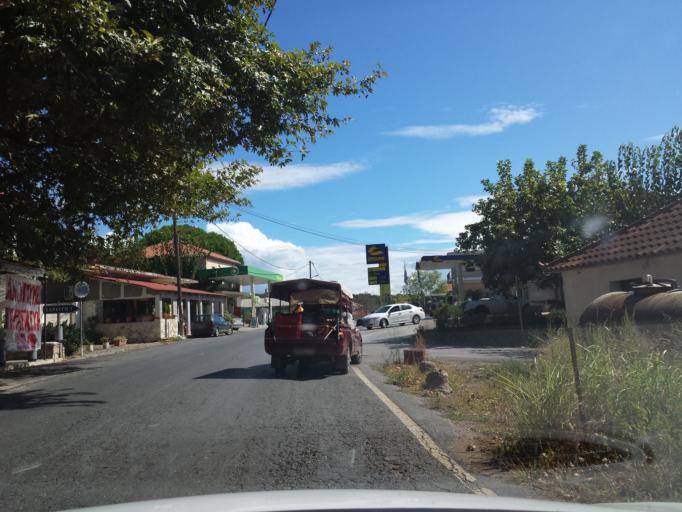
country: GR
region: Peloponnese
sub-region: Nomos Messinias
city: Vlakhopoulon
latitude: 37.0010
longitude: 21.8483
